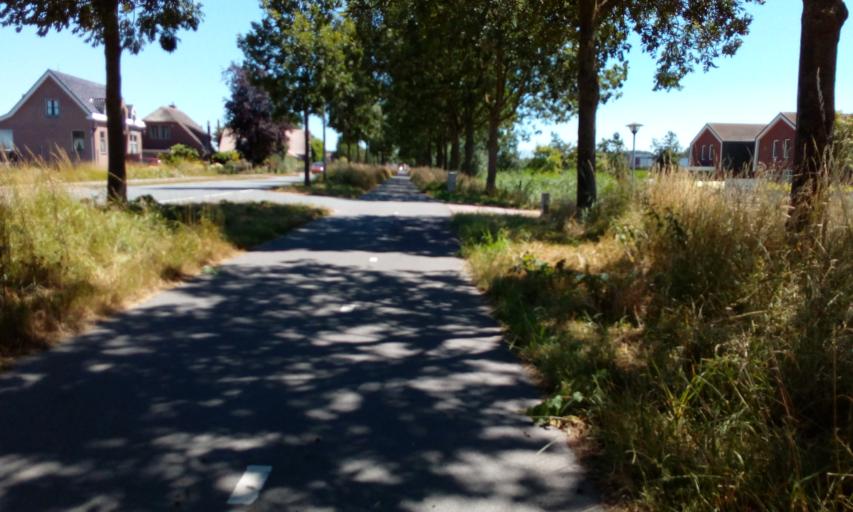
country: NL
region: South Holland
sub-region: Gemeente Alphen aan den Rijn
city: Alphen aan den Rijn
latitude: 52.1145
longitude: 4.6989
